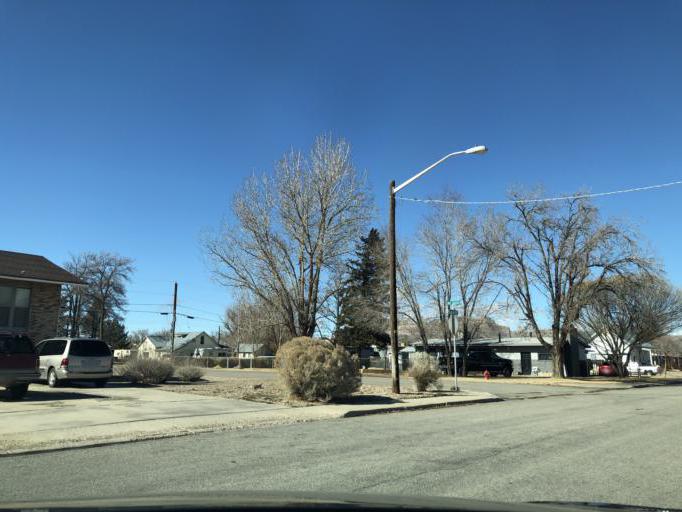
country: US
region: Utah
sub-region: Carbon County
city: East Carbon City
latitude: 38.9934
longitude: -110.1598
